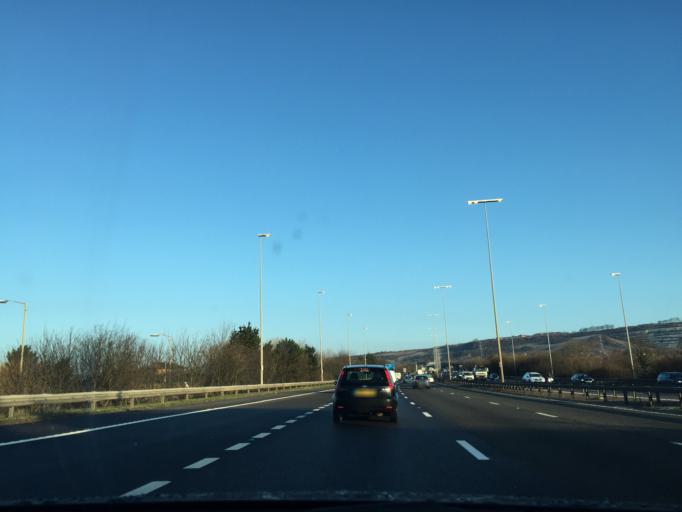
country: GB
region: England
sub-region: Portsmouth
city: Cosham
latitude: 50.8448
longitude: -1.0974
